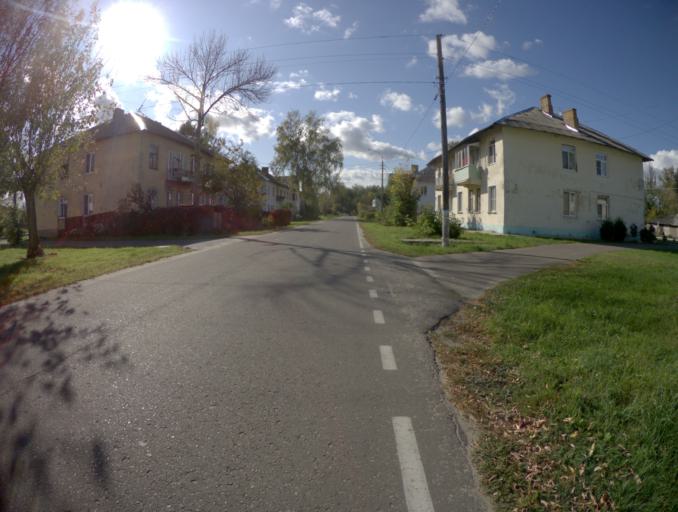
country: RU
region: Moskovskaya
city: Kerva
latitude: 55.6100
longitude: 39.5756
